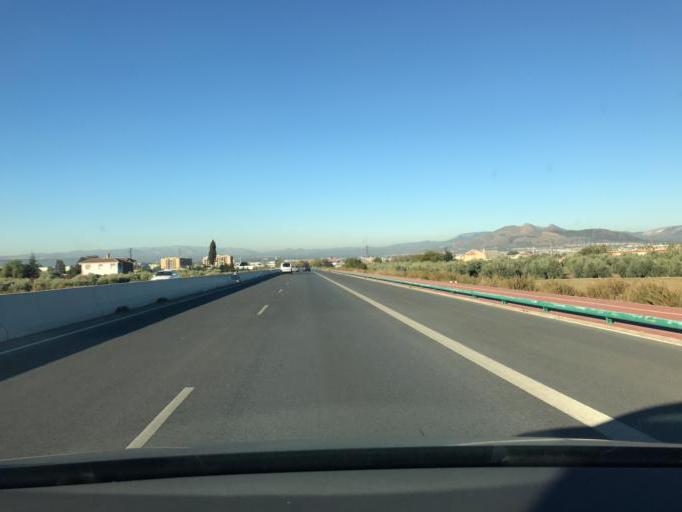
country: ES
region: Andalusia
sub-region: Provincia de Granada
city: Jun
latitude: 37.2136
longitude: -3.5991
